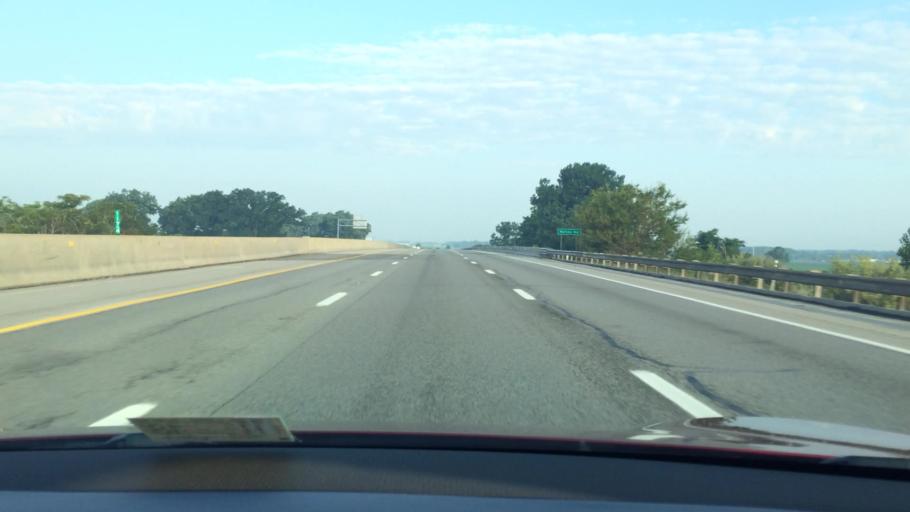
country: US
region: Ohio
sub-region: Erie County
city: Milan
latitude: 41.3254
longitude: -82.6297
